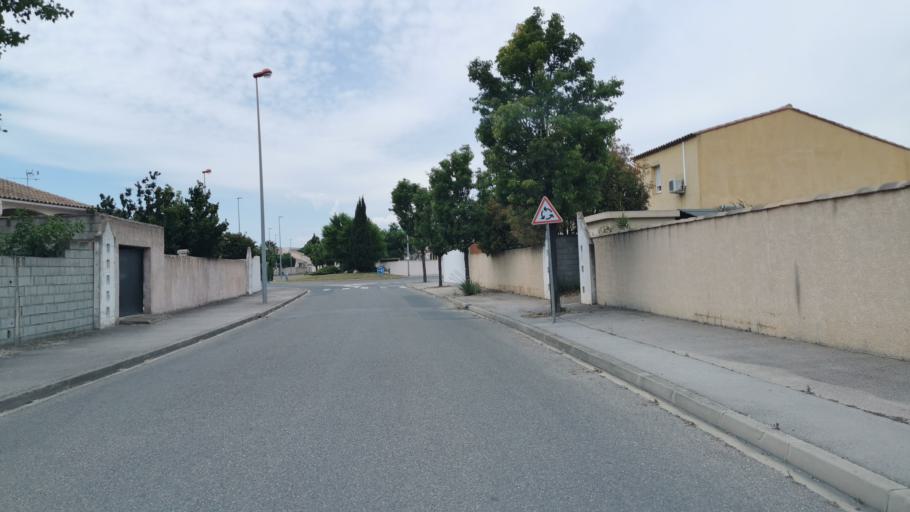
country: FR
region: Languedoc-Roussillon
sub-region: Departement de l'Aude
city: Narbonne
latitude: 43.1934
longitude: 3.0258
